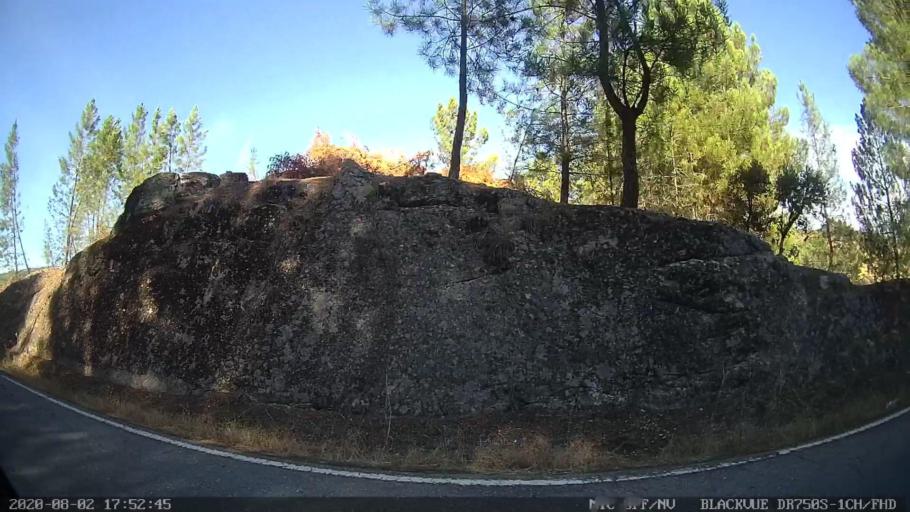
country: PT
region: Vila Real
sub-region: Murca
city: Murca
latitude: 41.4069
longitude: -7.4689
